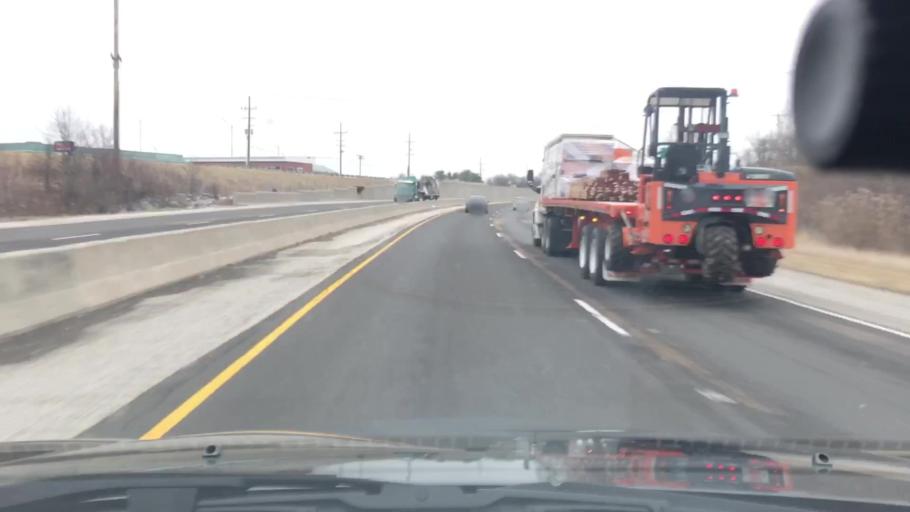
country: US
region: Illinois
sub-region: Madison County
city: Rosewood Heights
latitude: 38.8873
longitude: -90.0599
